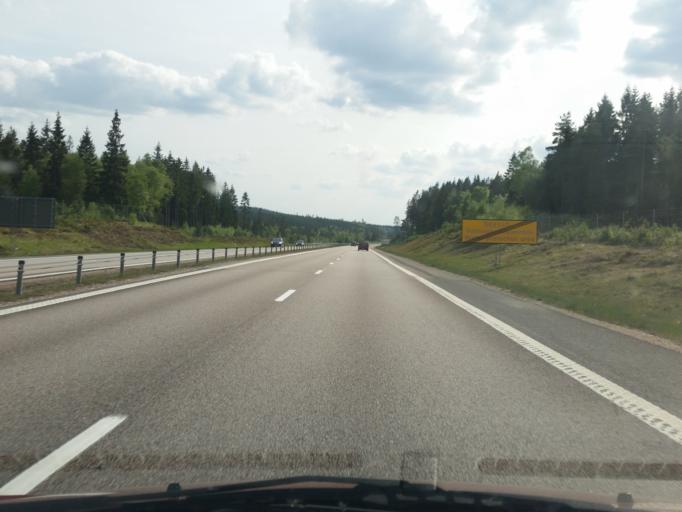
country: SE
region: Vaestra Goetaland
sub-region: Boras Kommun
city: Dalsjofors
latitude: 57.7489
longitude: 13.0709
